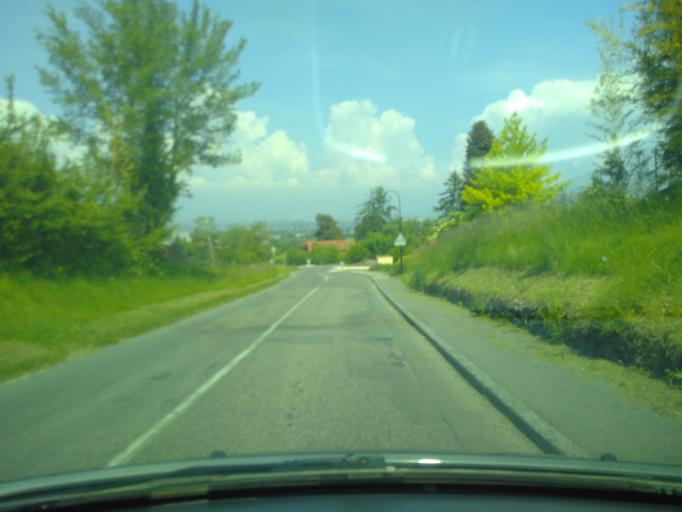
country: FR
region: Rhone-Alpes
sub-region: Departement de la Haute-Savoie
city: Archamps
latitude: 46.1317
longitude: 6.1326
